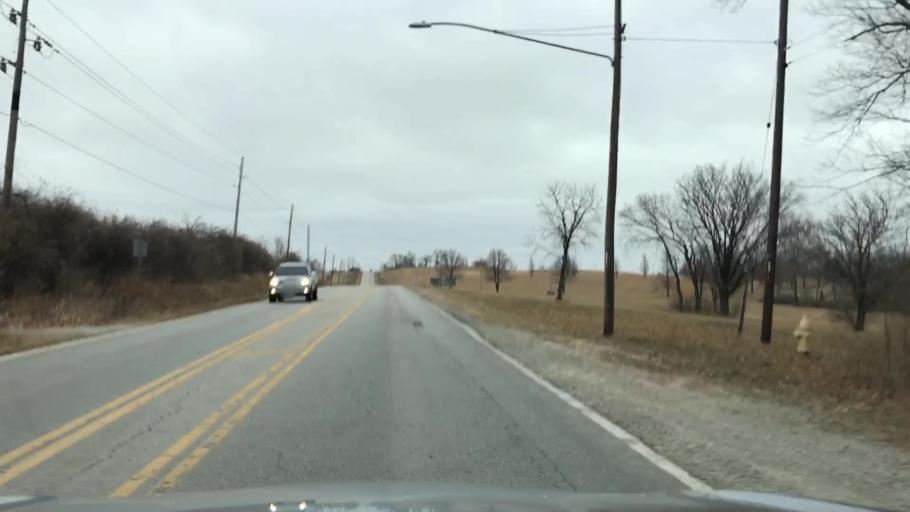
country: US
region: Missouri
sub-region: Clay County
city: Liberty
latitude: 39.2668
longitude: -94.4166
